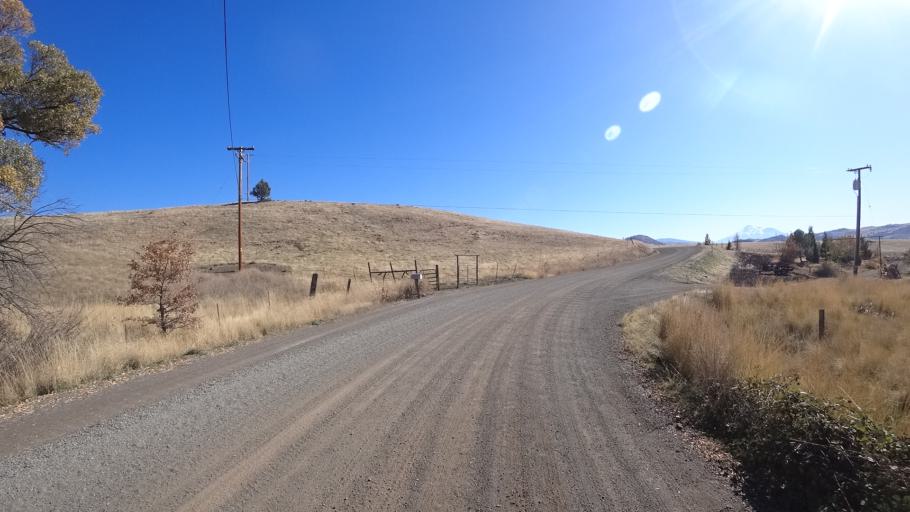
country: US
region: California
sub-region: Siskiyou County
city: Montague
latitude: 41.8319
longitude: -122.3880
